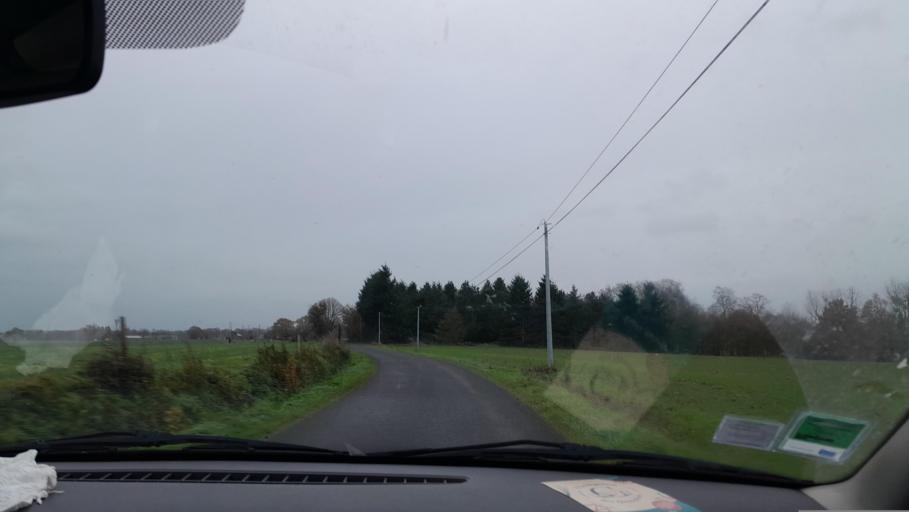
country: FR
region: Brittany
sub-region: Departement d'Ille-et-Vilaine
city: La Guerche-de-Bretagne
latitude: 47.9136
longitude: -1.1535
